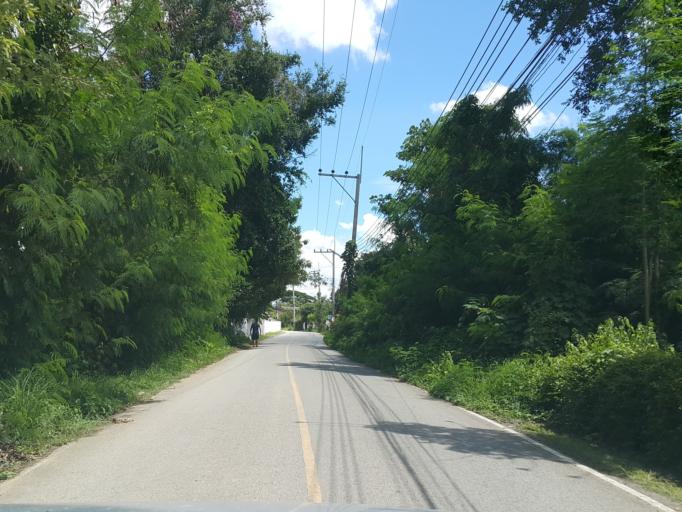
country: TH
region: Chiang Mai
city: San Kamphaeng
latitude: 18.7615
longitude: 99.1194
